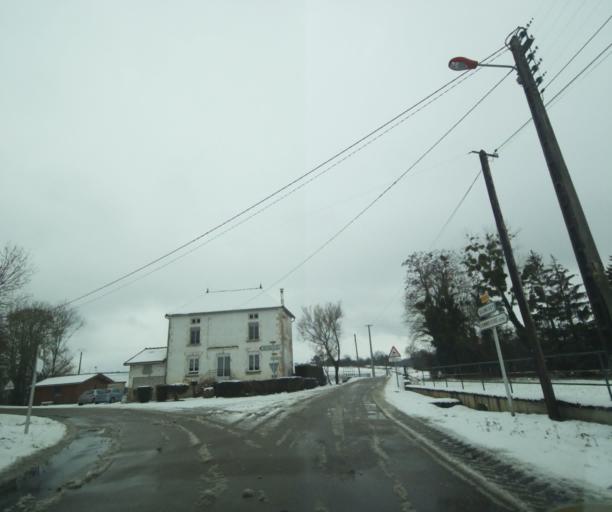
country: FR
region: Champagne-Ardenne
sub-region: Departement de la Haute-Marne
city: Laneuville-a-Remy
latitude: 48.4093
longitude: 4.8458
